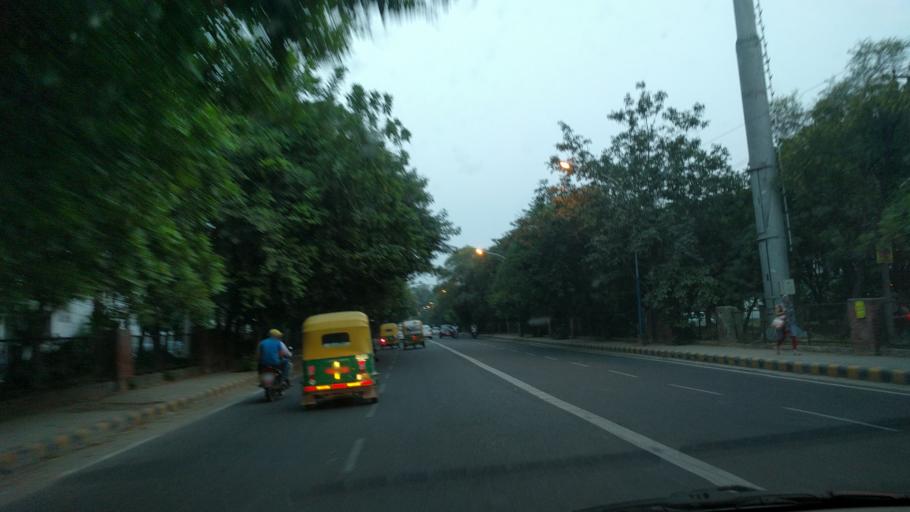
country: IN
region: Haryana
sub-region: Gurgaon
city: Gurgaon
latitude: 28.4517
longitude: 77.0614
